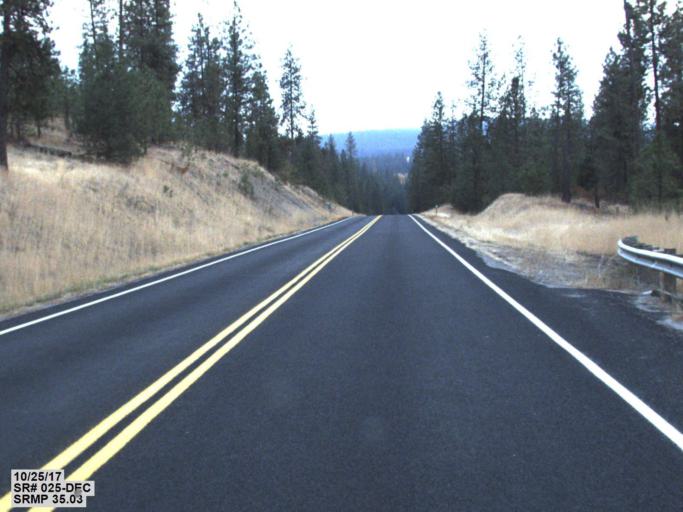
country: US
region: Washington
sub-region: Lincoln County
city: Davenport
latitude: 48.0355
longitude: -118.2300
